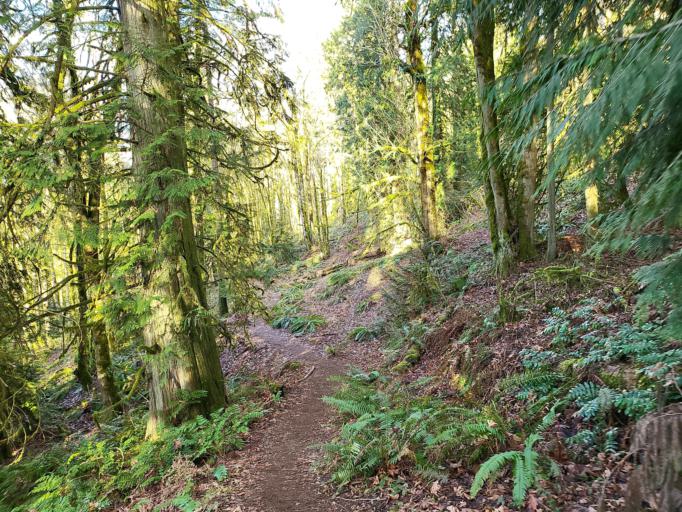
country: US
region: Washington
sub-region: King County
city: Issaquah
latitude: 47.5218
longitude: -122.0241
